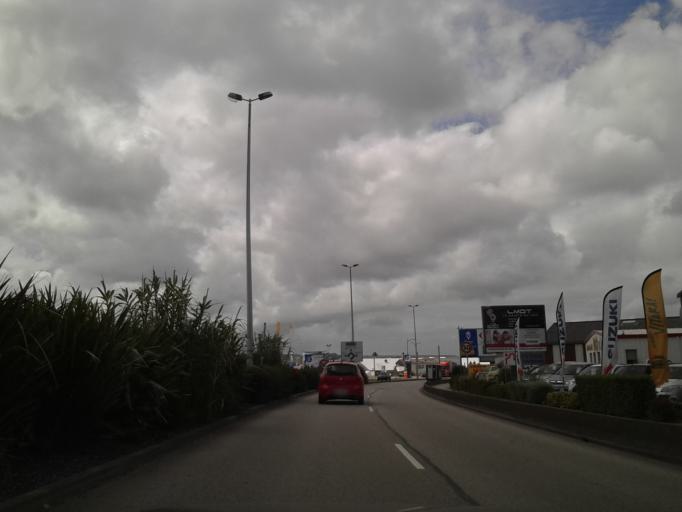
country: FR
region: Lower Normandy
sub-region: Departement de la Manche
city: Tourlaville
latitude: 49.6348
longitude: -1.5884
